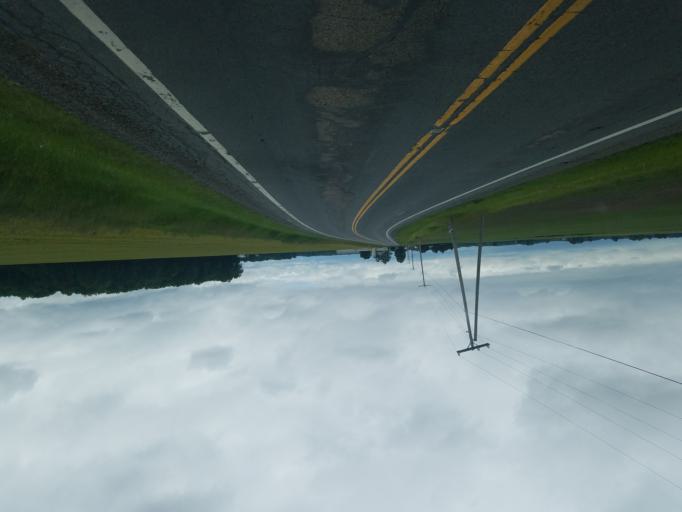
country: US
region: Ohio
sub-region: Crawford County
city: Bucyrus
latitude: 40.7745
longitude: -82.9166
